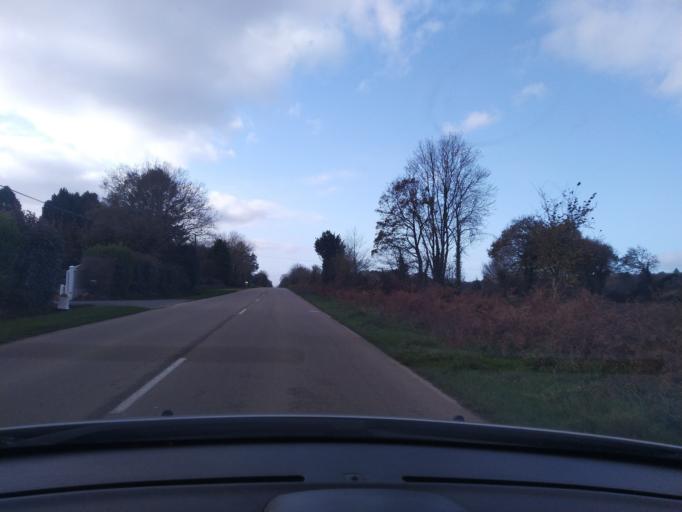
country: FR
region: Brittany
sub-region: Departement du Finistere
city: Plourin-les-Morlaix
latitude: 48.5765
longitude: -3.7739
